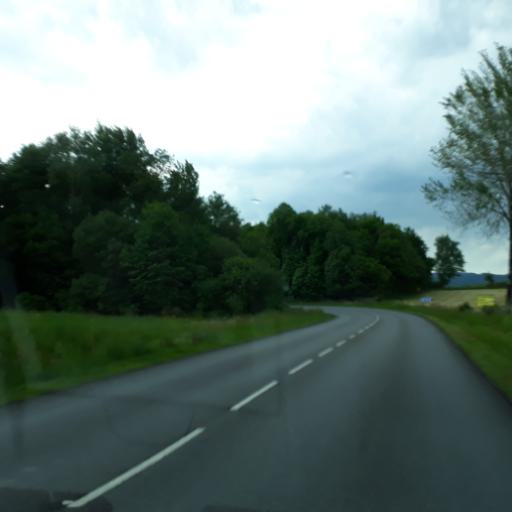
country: FR
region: Limousin
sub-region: Departement de la Haute-Vienne
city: Eymoutiers
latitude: 45.7647
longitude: 1.7499
